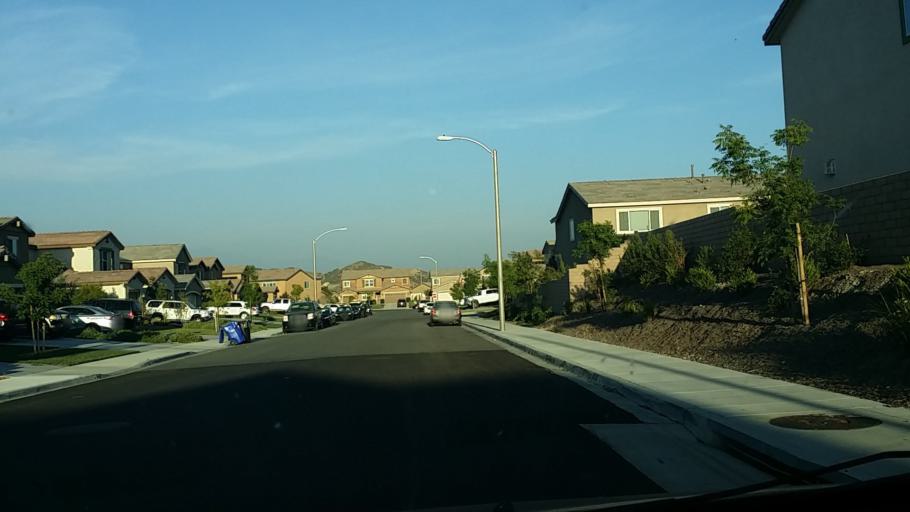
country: US
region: California
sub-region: San Bernardino County
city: Muscoy
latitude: 34.1898
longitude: -117.4118
